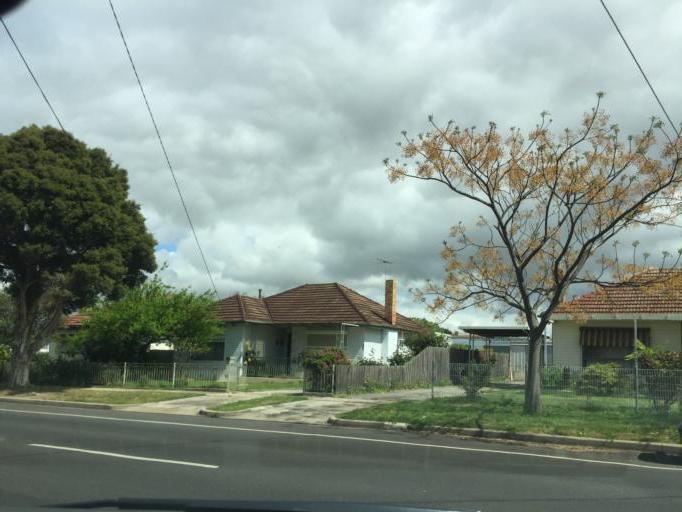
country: AU
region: Victoria
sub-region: Brimbank
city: Albion
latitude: -37.7685
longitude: 144.8423
